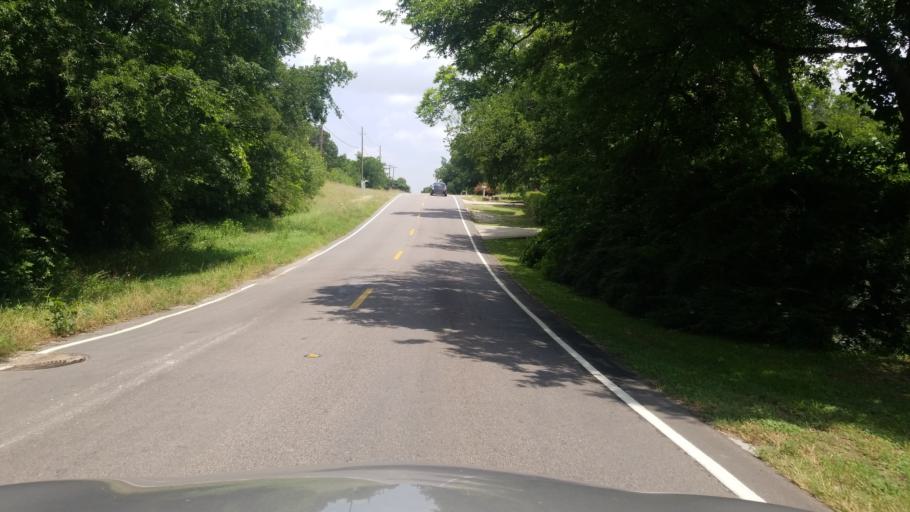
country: US
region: Texas
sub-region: Dallas County
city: Duncanville
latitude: 32.6744
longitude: -96.9256
